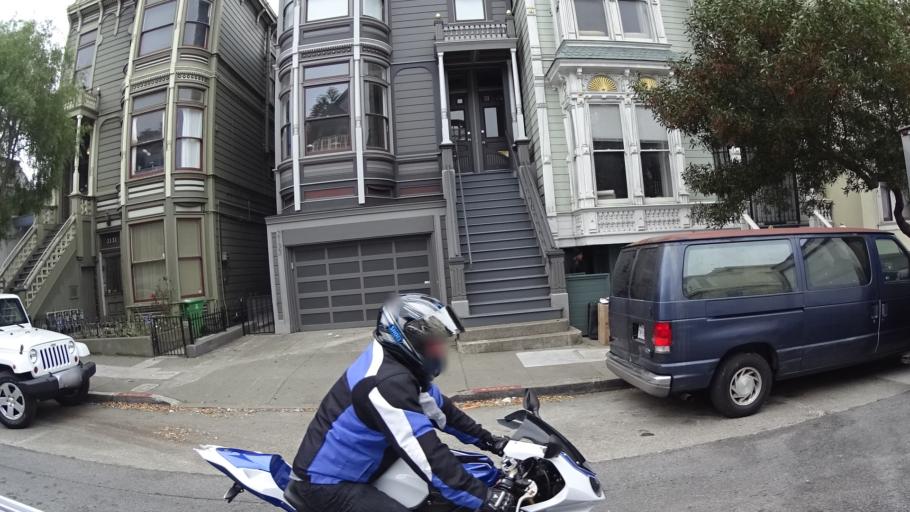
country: US
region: California
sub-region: San Francisco County
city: San Francisco
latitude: 37.7882
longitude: -122.4315
